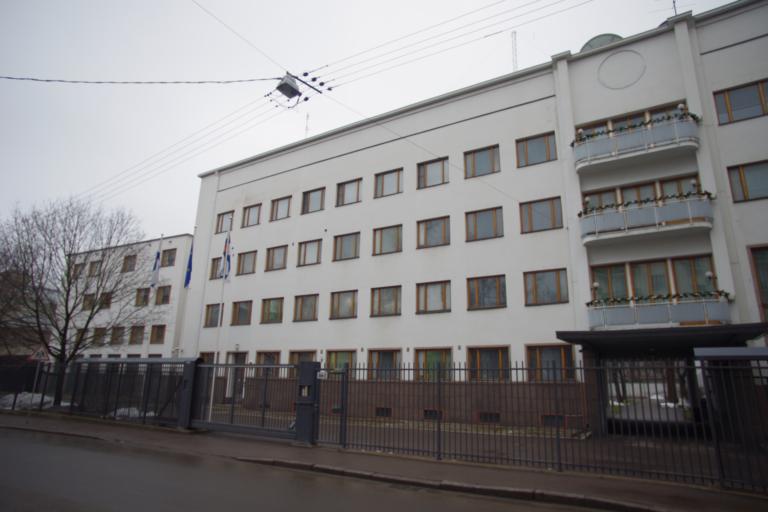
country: RU
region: Moskovskaya
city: Dorogomilovo
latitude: 55.7393
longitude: 37.5909
